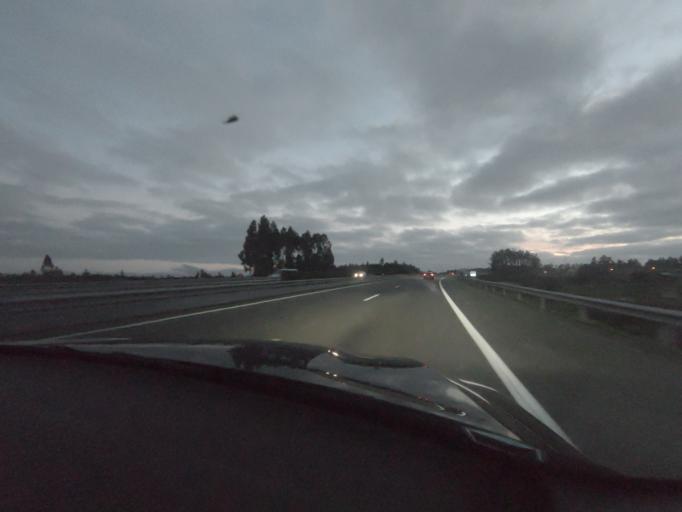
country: PT
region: Leiria
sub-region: Pombal
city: Pombal
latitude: 39.9492
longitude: -8.6704
